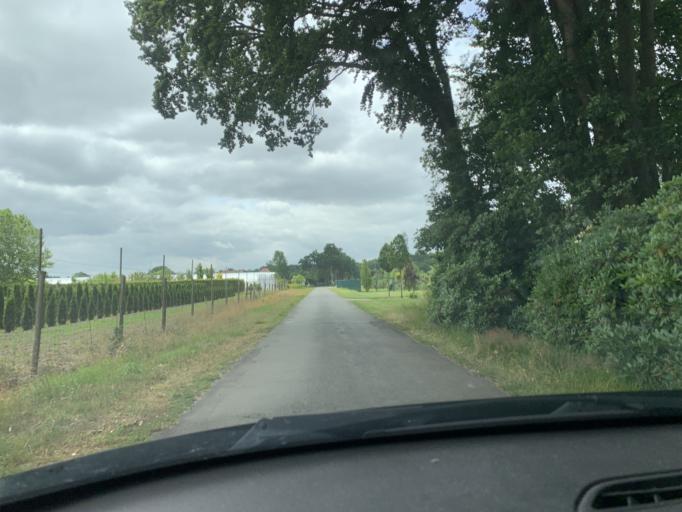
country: DE
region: Lower Saxony
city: Westerstede
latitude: 53.2619
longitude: 7.9726
